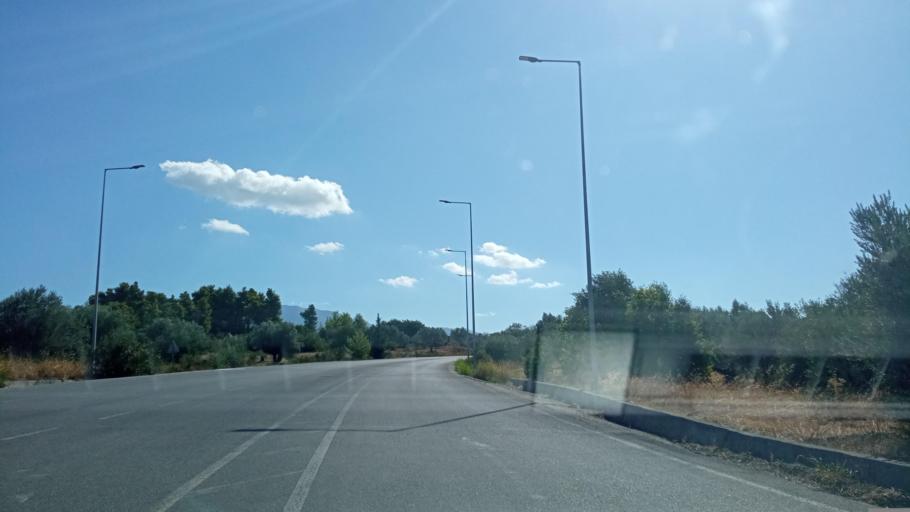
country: GR
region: Central Greece
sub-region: Nomos Evvoias
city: Psachna
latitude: 38.5799
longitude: 23.7690
